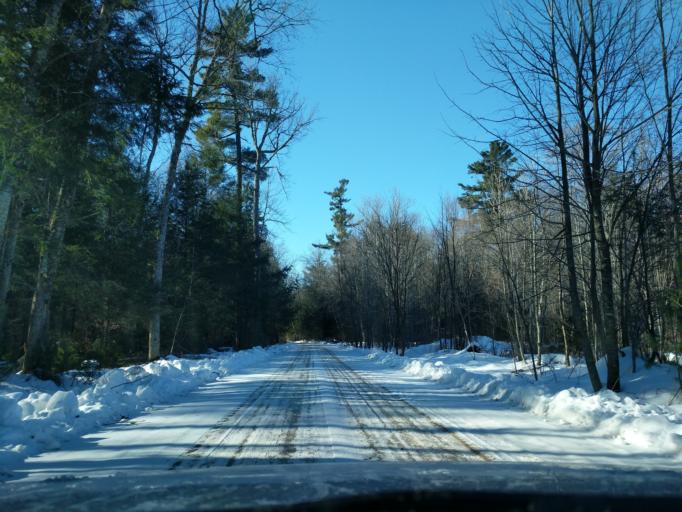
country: US
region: Wisconsin
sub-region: Menominee County
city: Keshena
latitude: 45.0981
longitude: -88.6101
